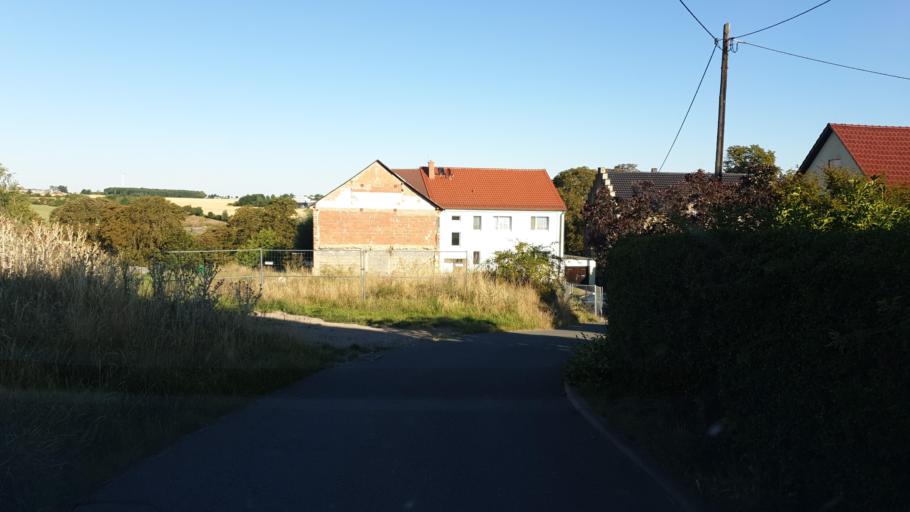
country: DE
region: Saxony
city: Lichtentanne
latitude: 50.6747
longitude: 12.4340
